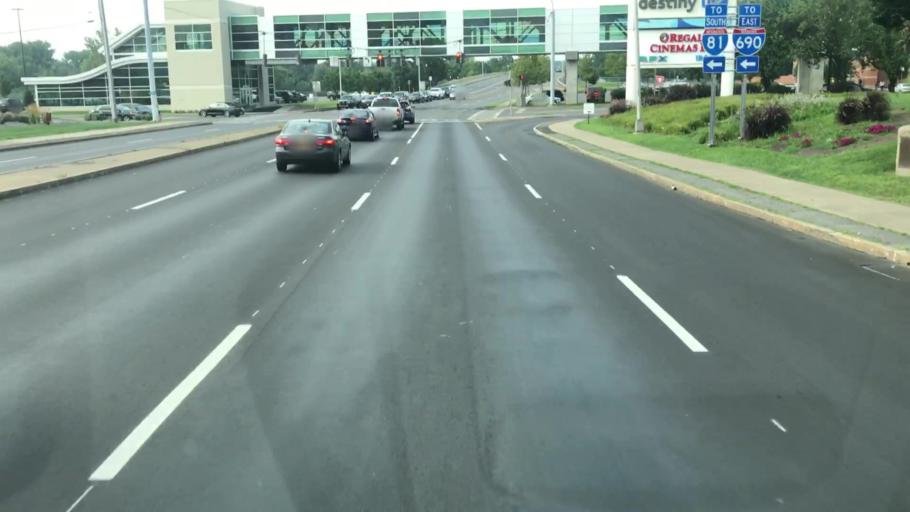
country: US
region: New York
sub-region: Onondaga County
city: Galeville
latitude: 43.0676
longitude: -76.1701
